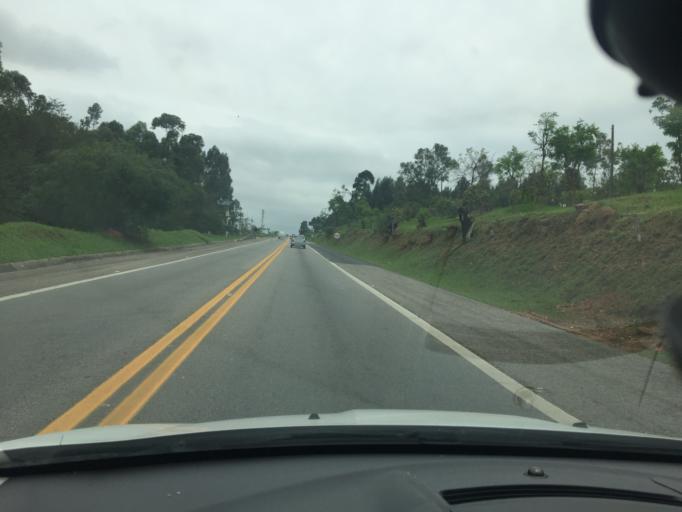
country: BR
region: Sao Paulo
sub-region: Jundiai
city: Jundiai
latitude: -23.1564
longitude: -46.8776
